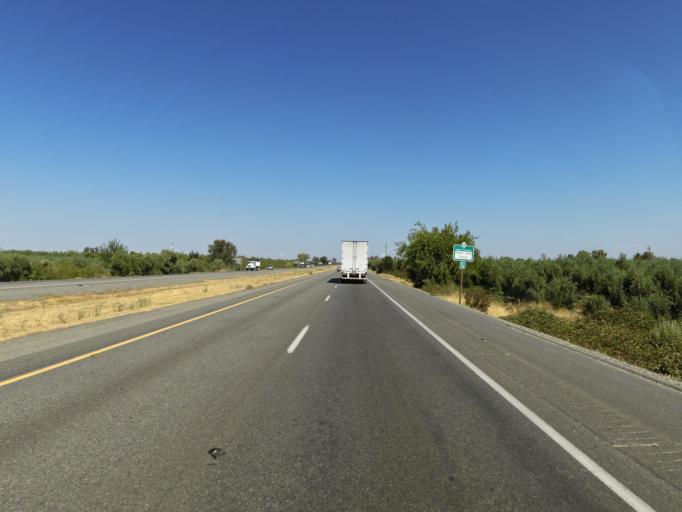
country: US
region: California
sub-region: Tehama County
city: Corning
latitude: 39.9157
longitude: -122.2000
